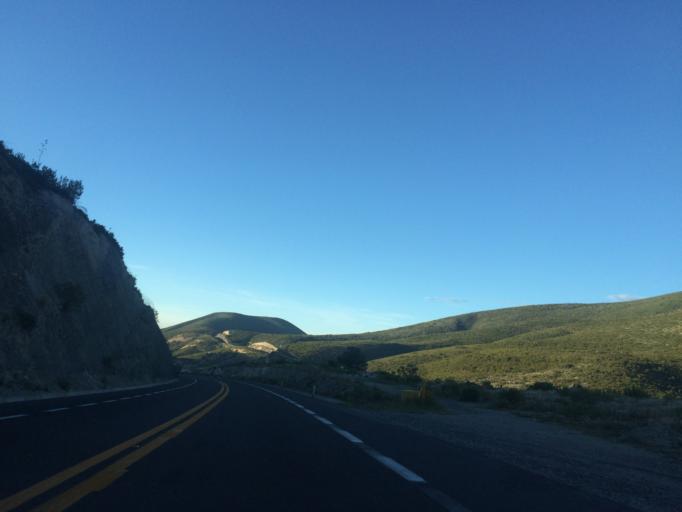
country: MX
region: Puebla
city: Chapuco
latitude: 18.6751
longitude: -97.4603
